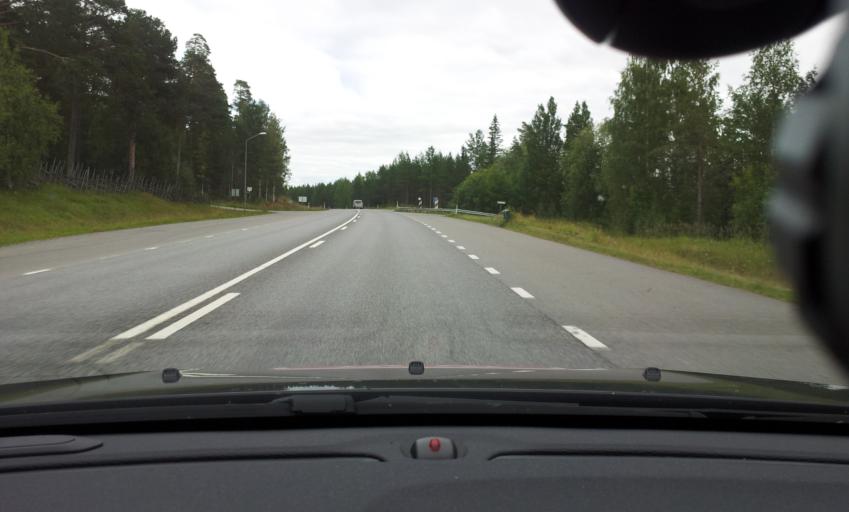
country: SE
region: Jaemtland
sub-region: Krokoms Kommun
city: Krokom
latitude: 63.3154
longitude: 14.0956
